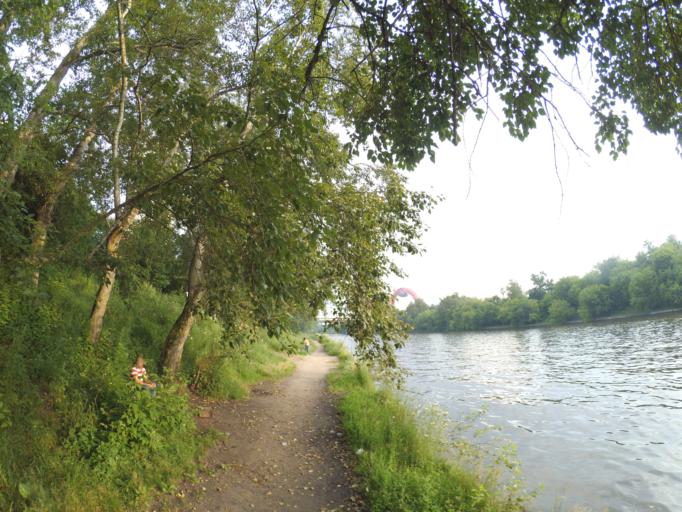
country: RU
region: Moscow
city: Shchukino
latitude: 55.7830
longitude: 37.4465
